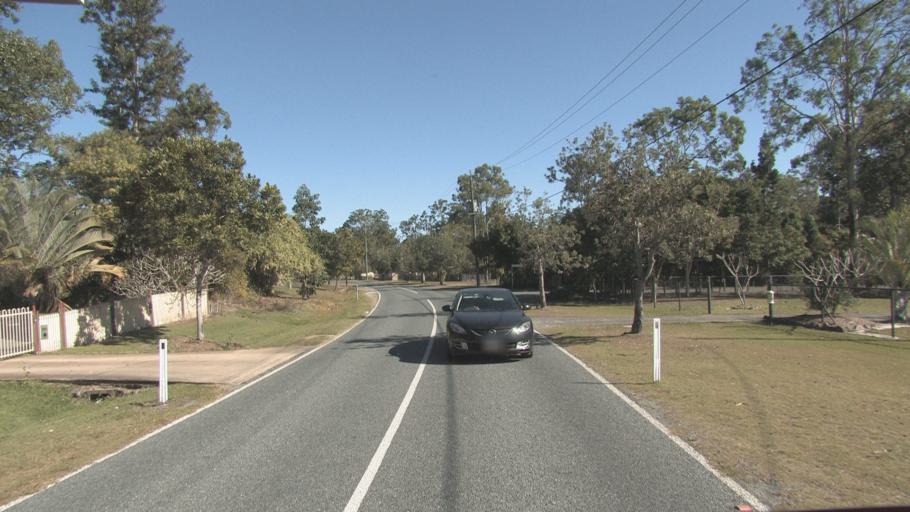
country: AU
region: Queensland
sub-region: Logan
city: North Maclean
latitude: -27.7418
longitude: 152.9568
